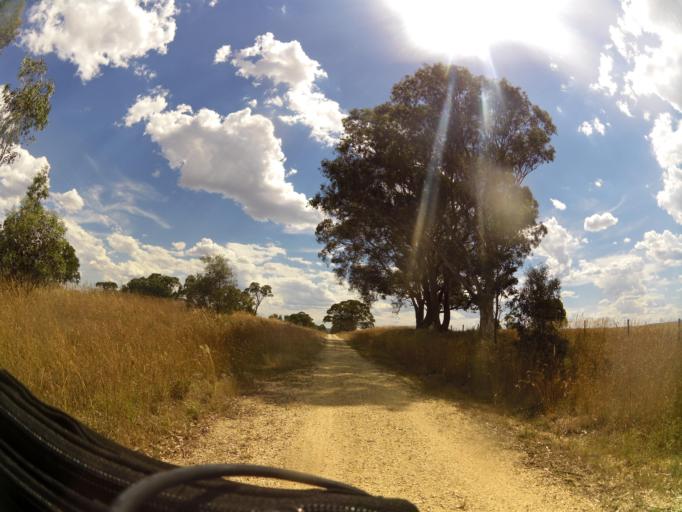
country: AU
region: Victoria
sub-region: Wellington
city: Heyfield
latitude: -37.9788
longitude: 146.7480
